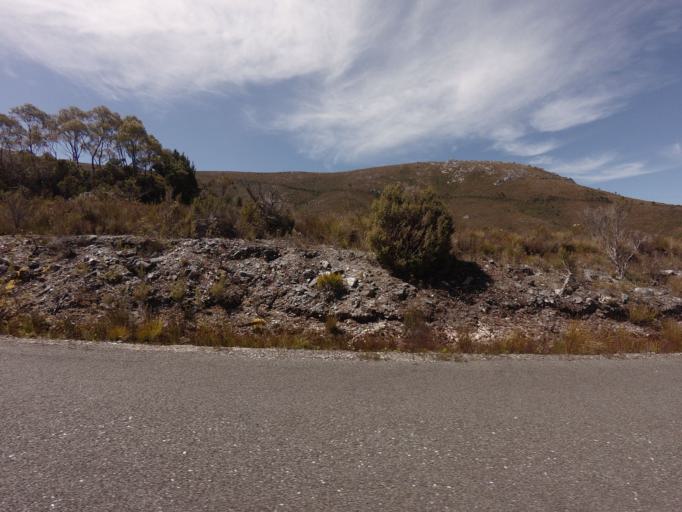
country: AU
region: Tasmania
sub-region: West Coast
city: Queenstown
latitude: -42.7891
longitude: 146.0627
